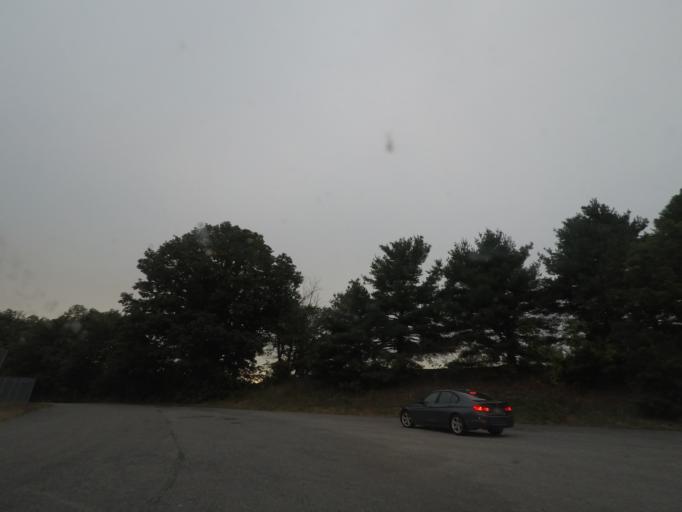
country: US
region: Connecticut
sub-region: Windham County
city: Thompson
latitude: 41.9833
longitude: -71.8267
